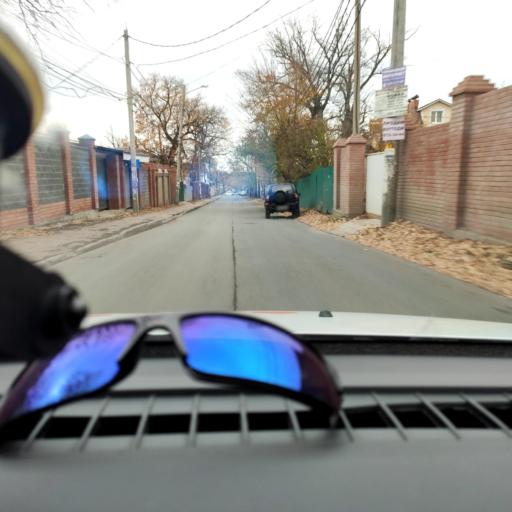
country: RU
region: Samara
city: Samara
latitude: 53.2555
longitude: 50.1913
